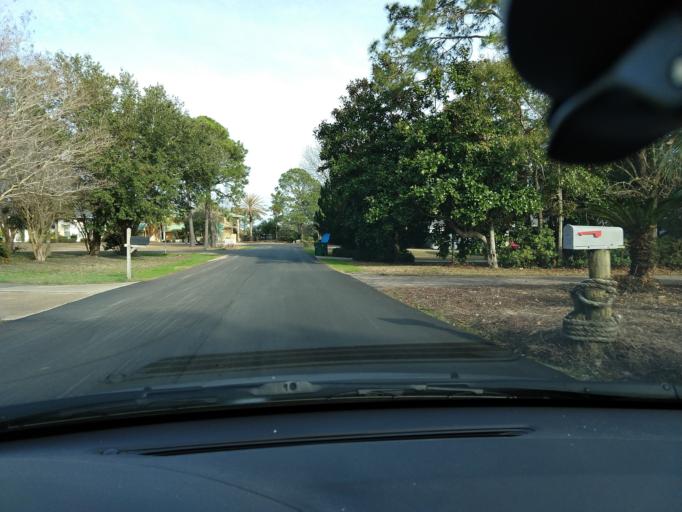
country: US
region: Florida
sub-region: Santa Rosa County
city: Woodlawn Beach
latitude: 30.3969
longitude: -86.9406
